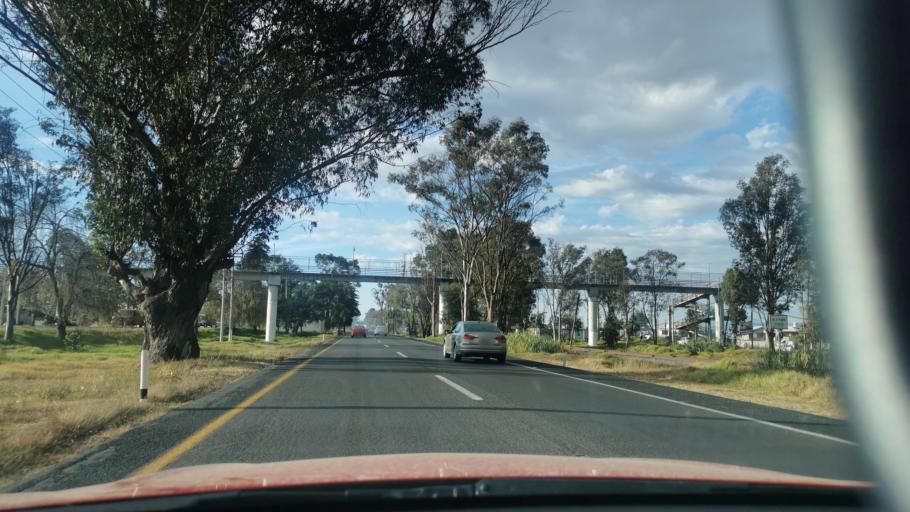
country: MX
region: Mexico
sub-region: Toluca
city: Colonia Aviacion Autopan
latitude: 19.3746
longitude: -99.6990
